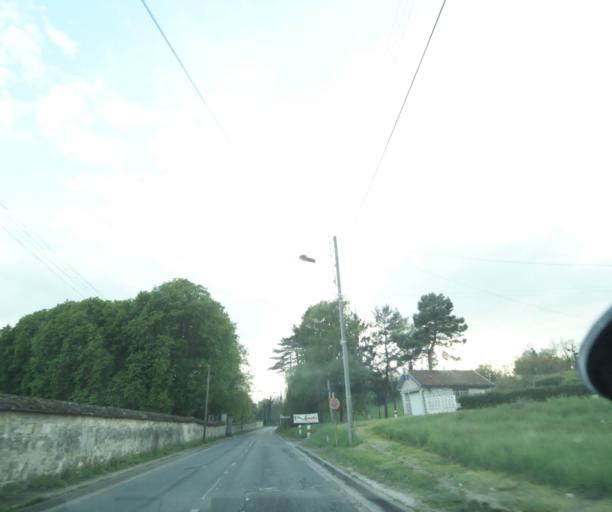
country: FR
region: Ile-de-France
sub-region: Departement de Seine-et-Marne
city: Montigny-sur-Loing
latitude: 48.3396
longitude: 2.7652
